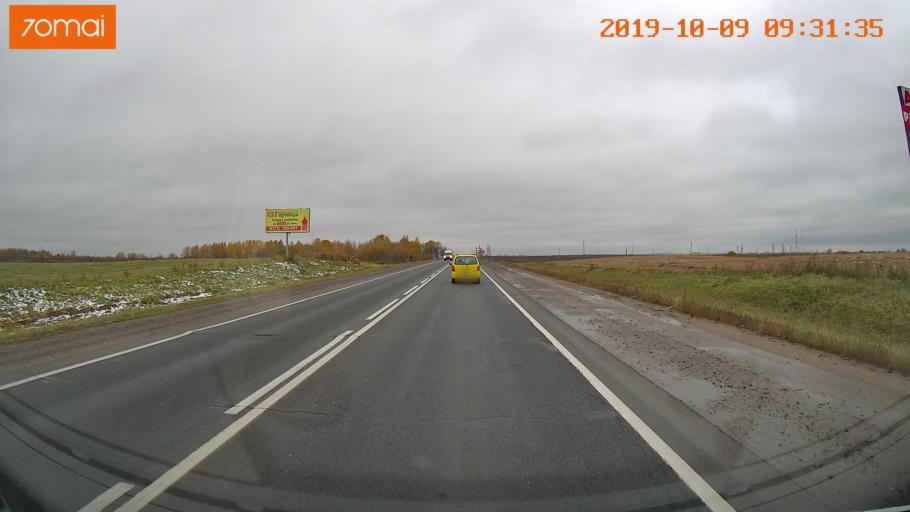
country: RU
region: Vologda
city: Vologda
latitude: 59.1506
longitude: 39.9375
